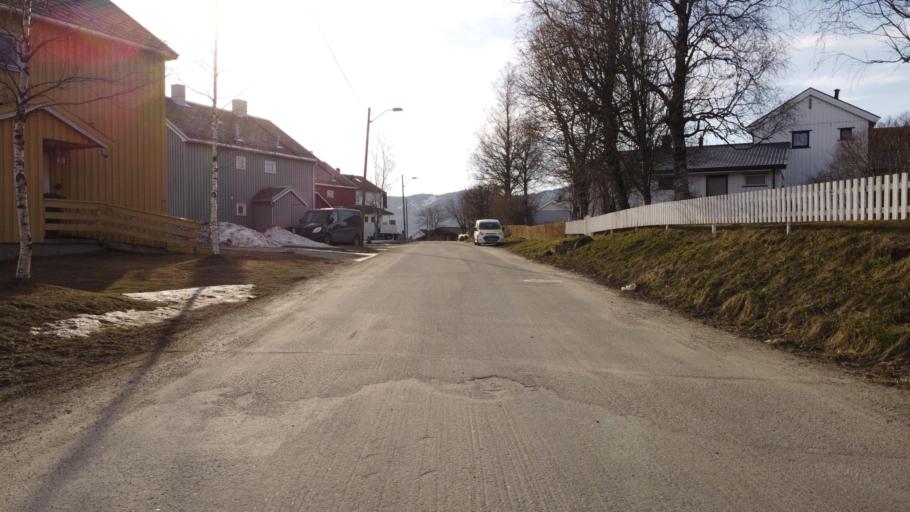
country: NO
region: Nordland
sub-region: Rana
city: Mo i Rana
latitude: 66.3147
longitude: 14.1440
